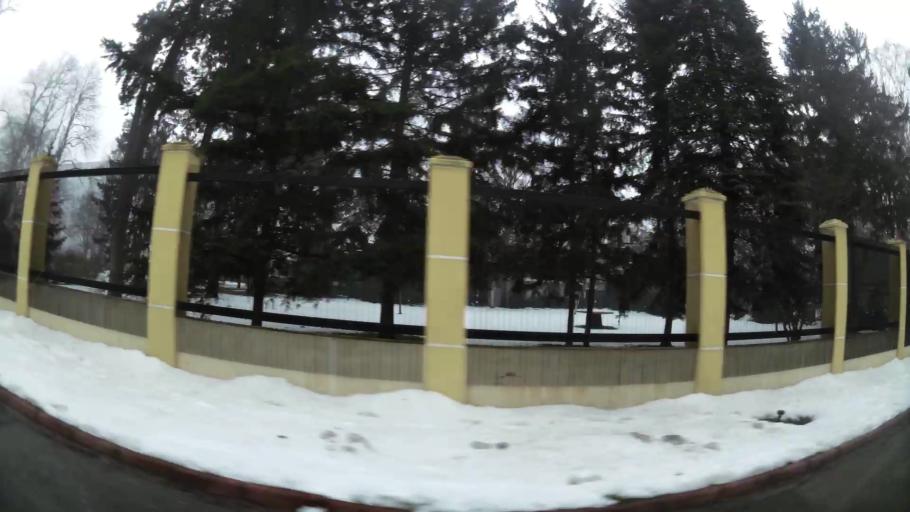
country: RS
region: Central Serbia
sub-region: Belgrade
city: Savski Venac
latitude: 44.7825
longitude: 20.4545
